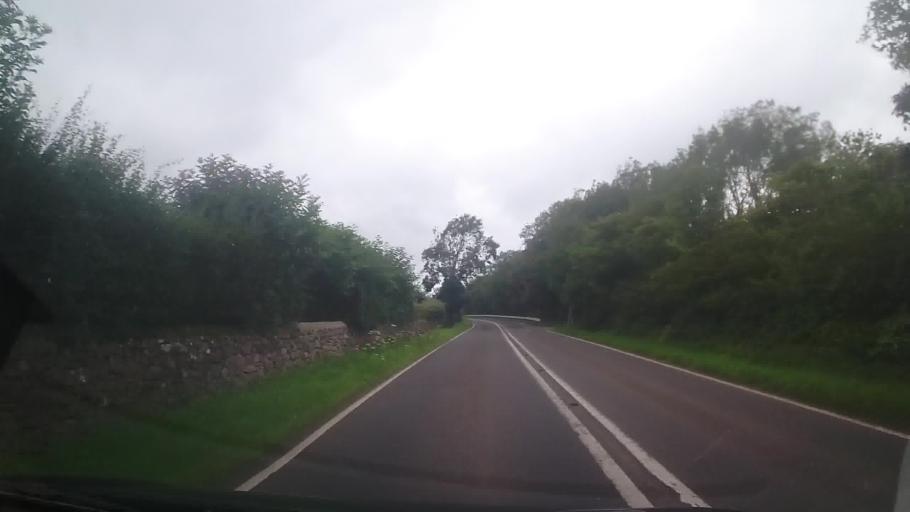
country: GB
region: Wales
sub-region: Gwynedd
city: Y Felinheli
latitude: 53.1936
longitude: -4.2416
